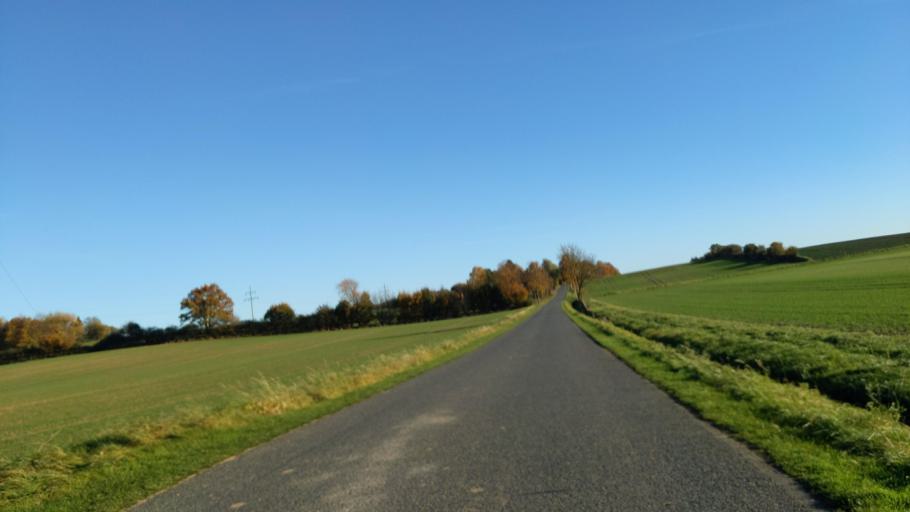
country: DE
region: Schleswig-Holstein
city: Gross Disnack
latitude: 53.7430
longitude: 10.6984
